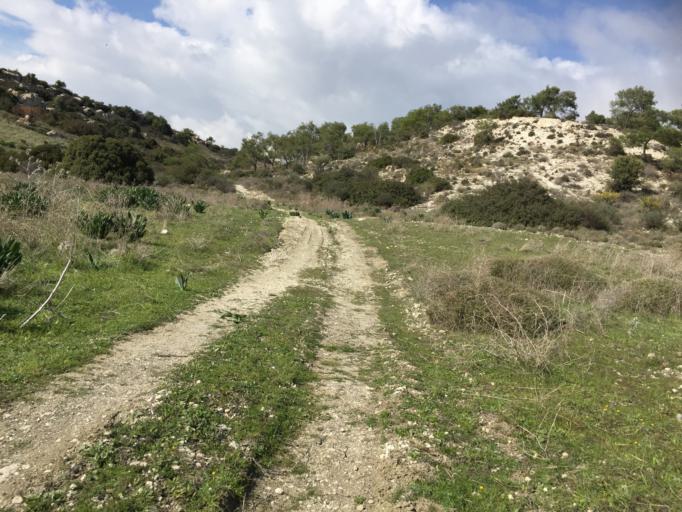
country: CY
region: Larnaka
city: Agios Tychon
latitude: 34.7432
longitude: 33.1390
